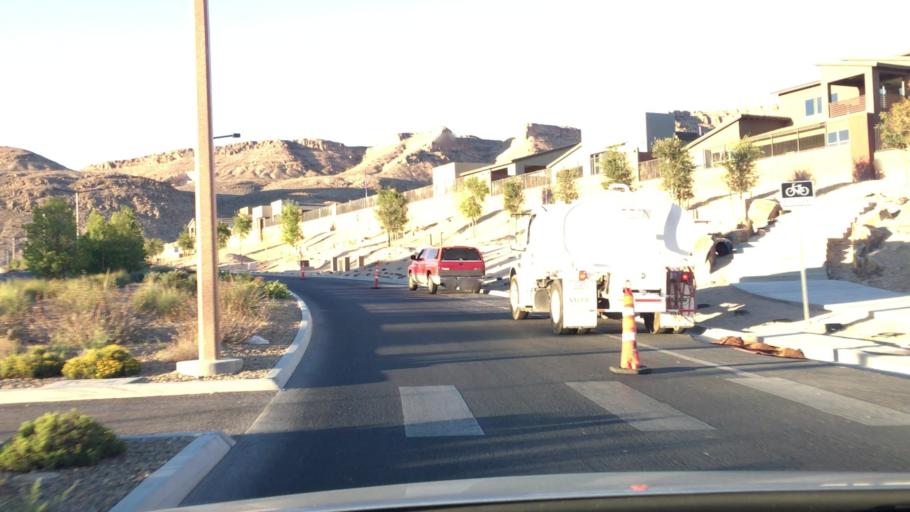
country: US
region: Nevada
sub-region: Clark County
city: Summerlin South
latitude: 36.0668
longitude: -115.3157
